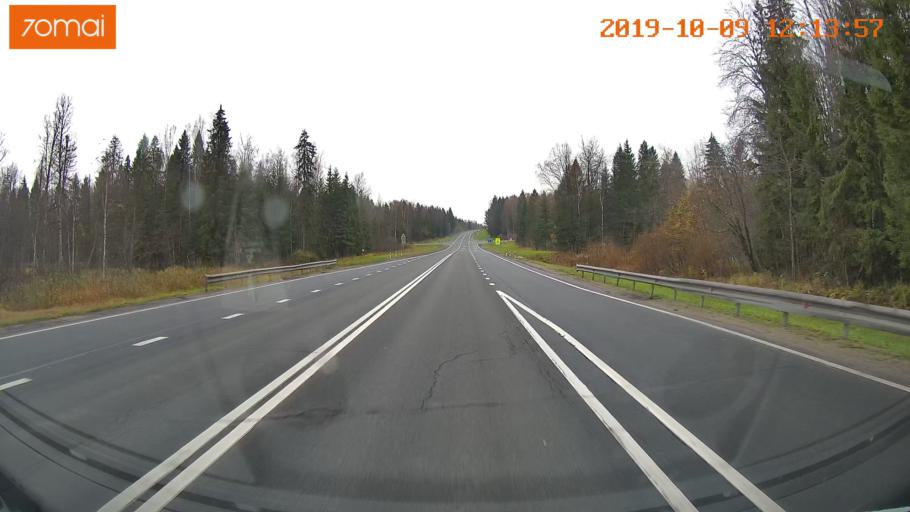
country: RU
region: Jaroslavl
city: Prechistoye
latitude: 58.5026
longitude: 40.3422
